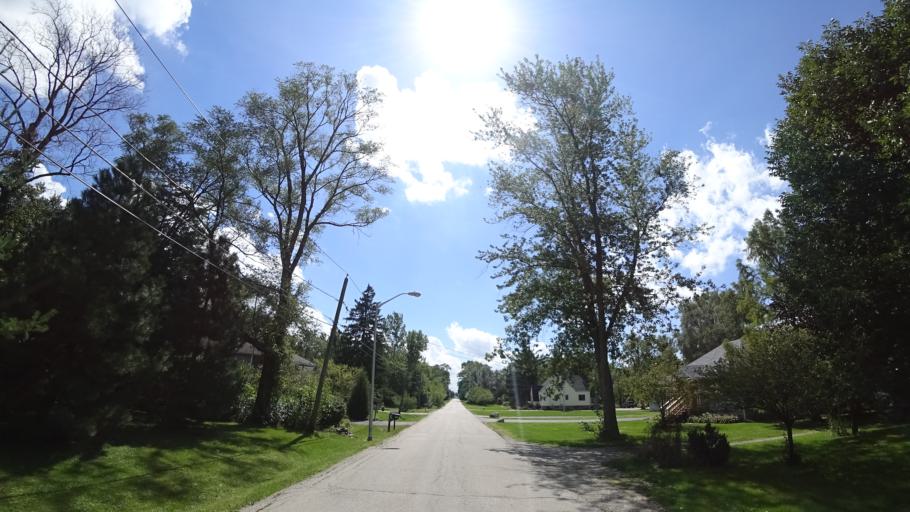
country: US
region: Illinois
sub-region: Cook County
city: Tinley Park
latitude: 41.5652
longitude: -87.7885
